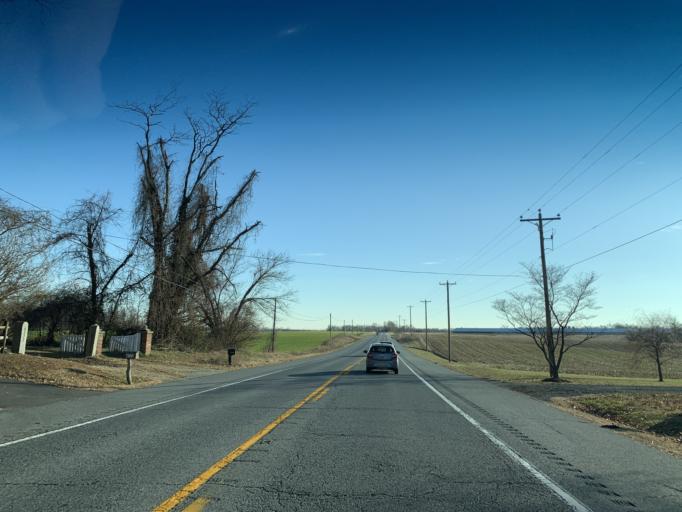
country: US
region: Delaware
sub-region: New Castle County
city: Middletown
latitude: 39.4541
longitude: -75.8703
